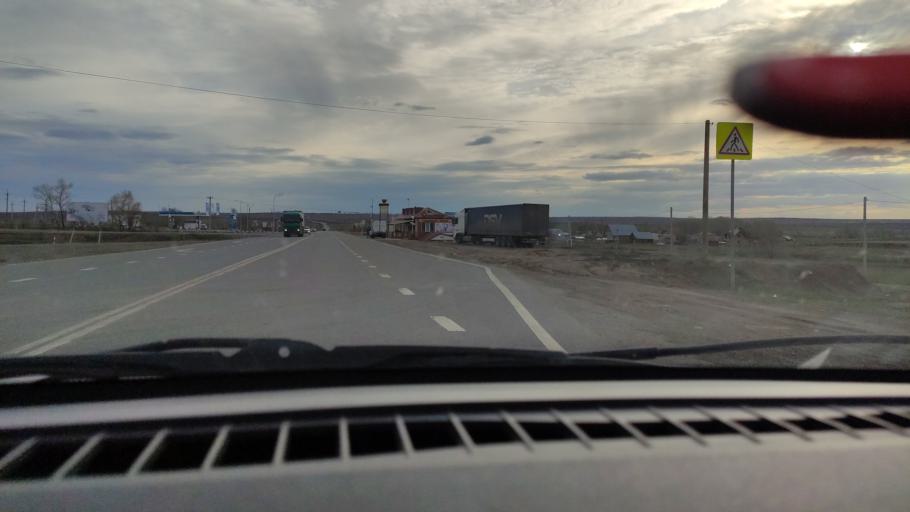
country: RU
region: Orenburg
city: Tatarskaya Kargala
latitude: 52.0286
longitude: 55.2333
